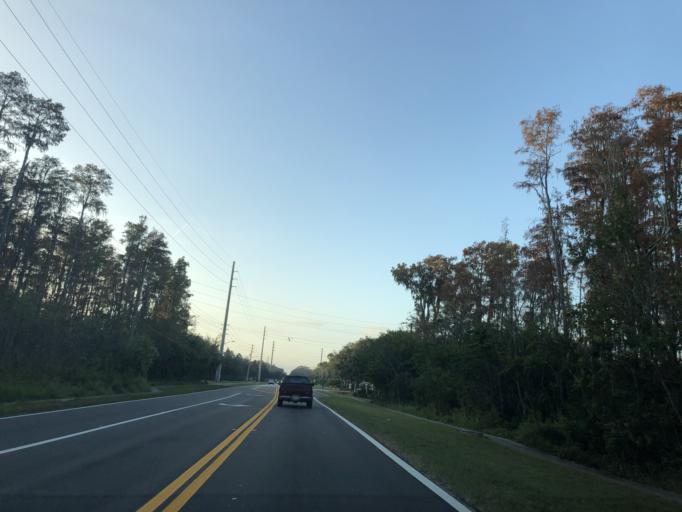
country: US
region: Florida
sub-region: Osceola County
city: Kissimmee
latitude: 28.3160
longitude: -81.4452
